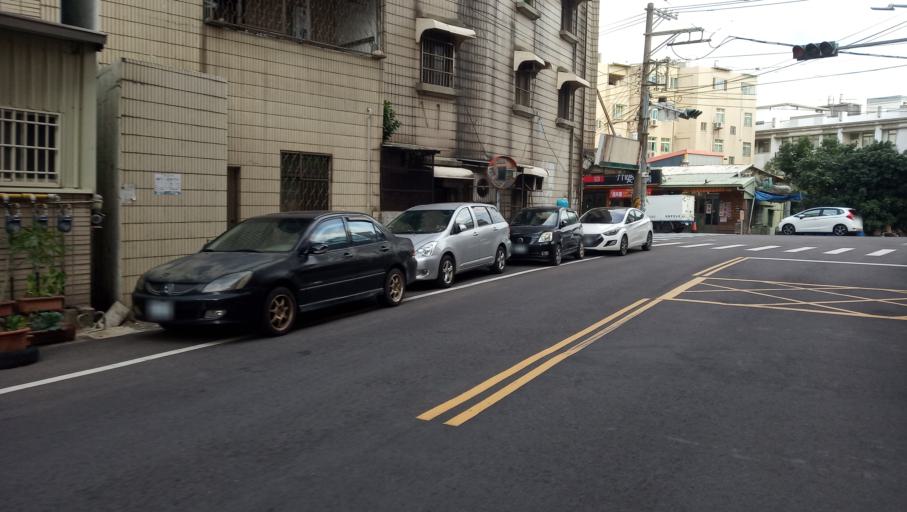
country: TW
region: Taiwan
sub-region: Hsinchu
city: Hsinchu
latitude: 24.7958
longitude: 120.9542
